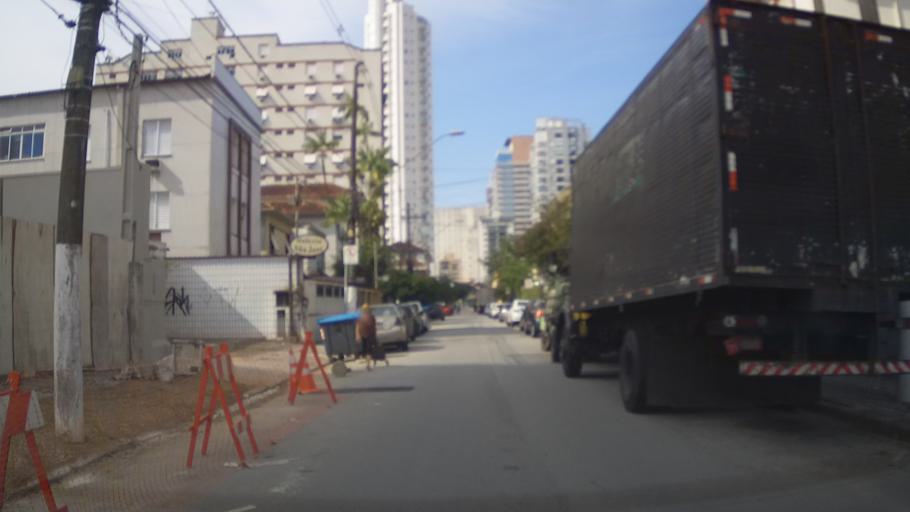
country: BR
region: Sao Paulo
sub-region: Santos
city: Santos
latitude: -23.9596
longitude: -46.3307
